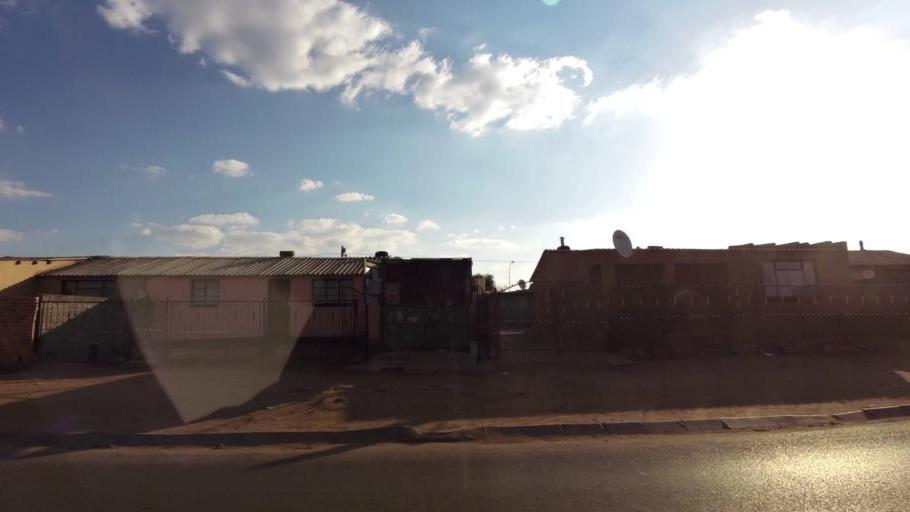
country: ZA
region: Gauteng
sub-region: City of Johannesburg Metropolitan Municipality
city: Soweto
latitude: -26.2343
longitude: 27.9017
